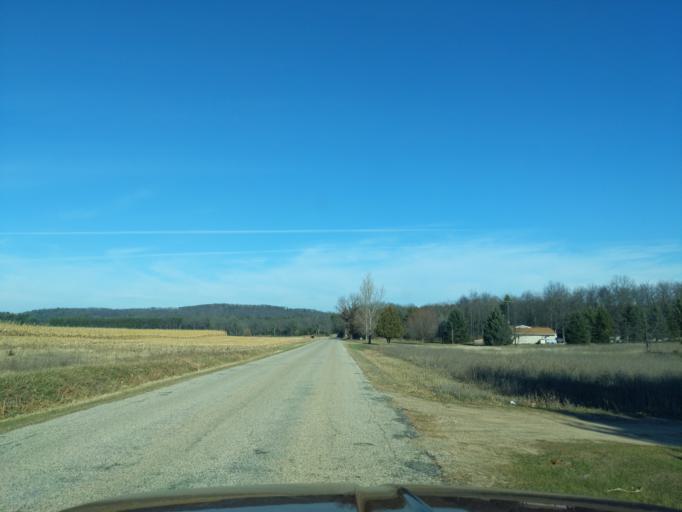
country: US
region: Wisconsin
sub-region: Waushara County
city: Silver Lake
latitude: 44.0995
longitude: -89.1788
